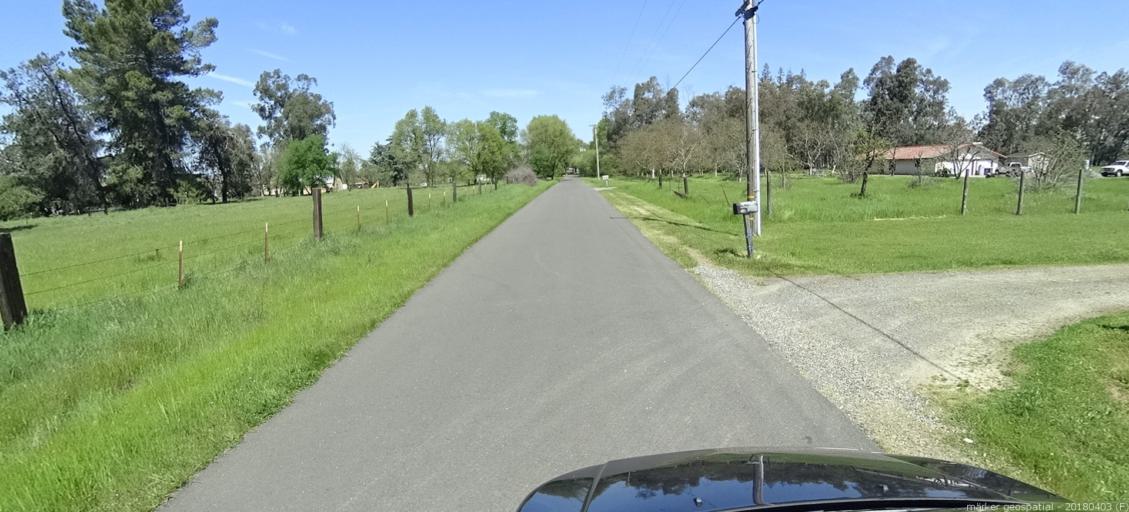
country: US
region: California
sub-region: Sacramento County
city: Wilton
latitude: 38.4031
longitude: -121.2780
